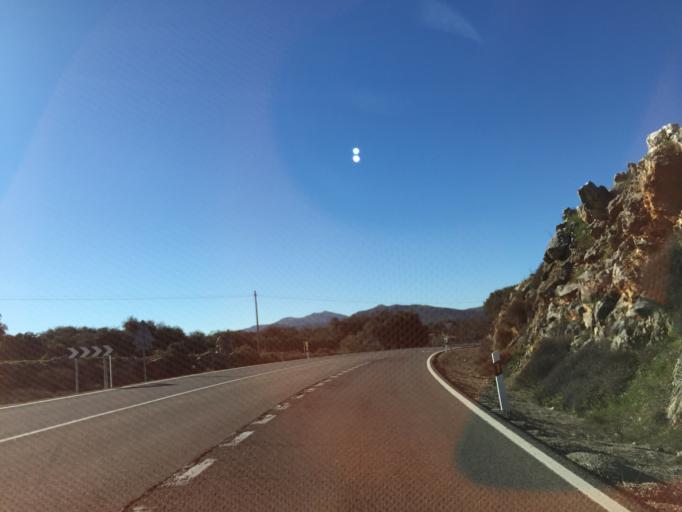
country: ES
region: Andalusia
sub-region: Provincia de Malaga
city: Cuevas del Becerro
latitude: 36.8493
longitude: -5.0556
